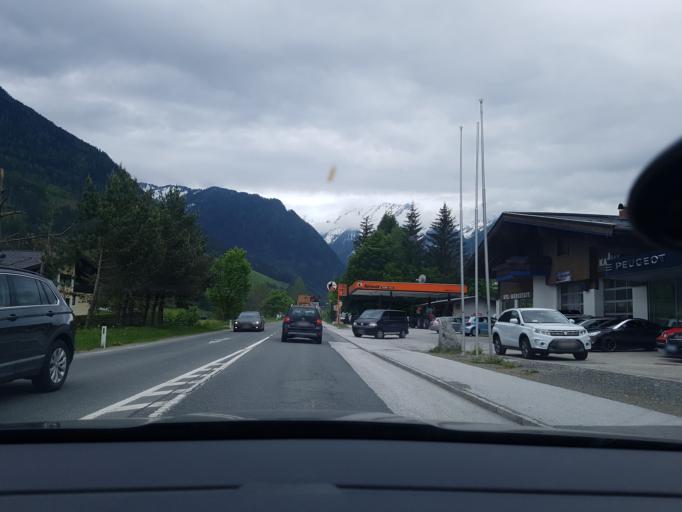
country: AT
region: Salzburg
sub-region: Politischer Bezirk Zell am See
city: Neukirchen am Grossvenediger
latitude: 47.2523
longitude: 12.2792
